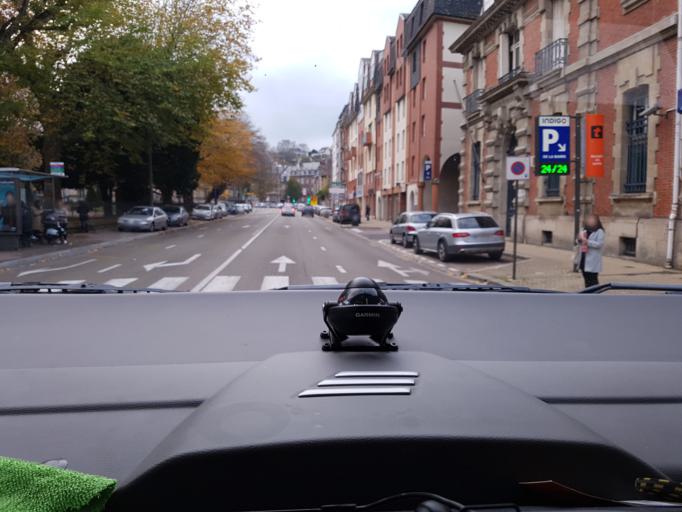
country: FR
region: Haute-Normandie
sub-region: Departement de la Seine-Maritime
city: Dieppe
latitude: 49.9234
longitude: 1.0755
